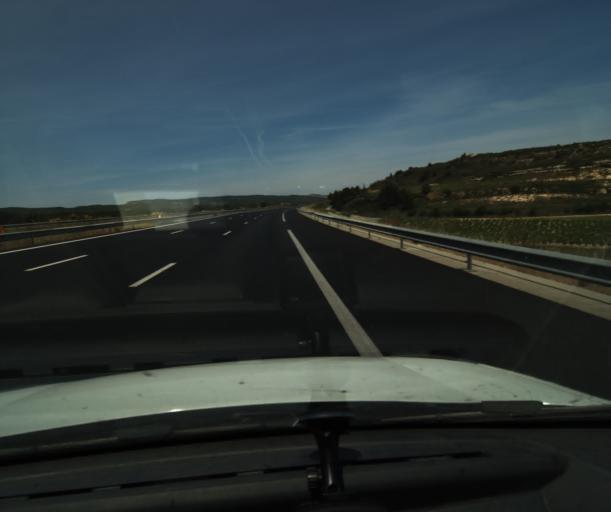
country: FR
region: Languedoc-Roussillon
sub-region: Departement de l'Aude
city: Peyriac-de-Mer
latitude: 43.0790
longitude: 2.9362
